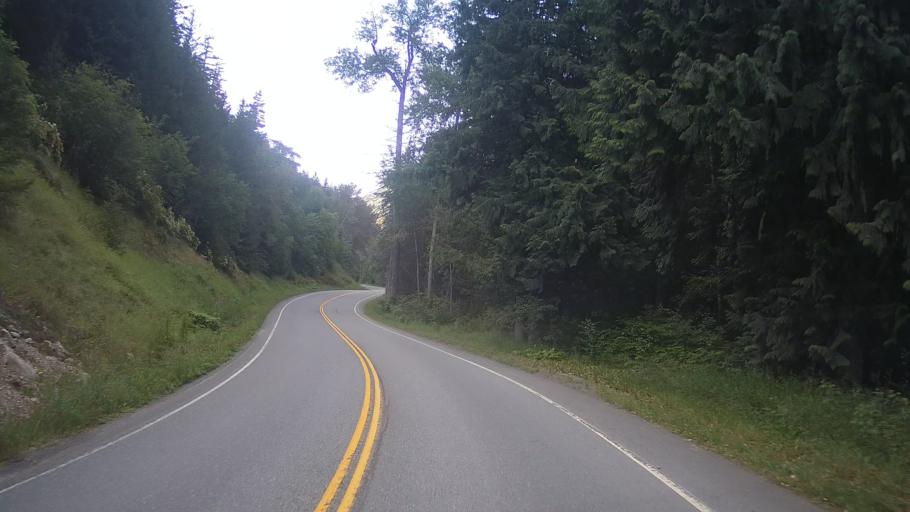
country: CA
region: British Columbia
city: Lillooet
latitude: 50.6199
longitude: -122.1034
